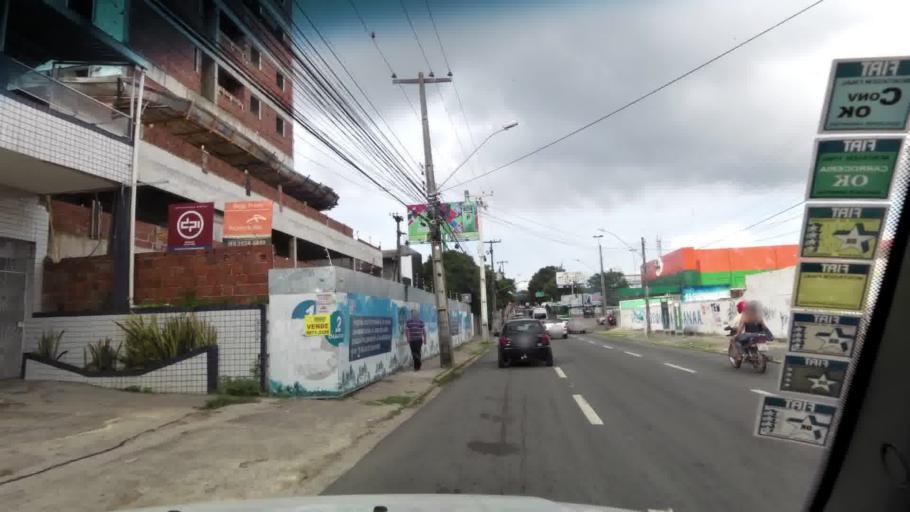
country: BR
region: Pernambuco
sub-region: Recife
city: Recife
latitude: -8.1327
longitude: -34.9103
